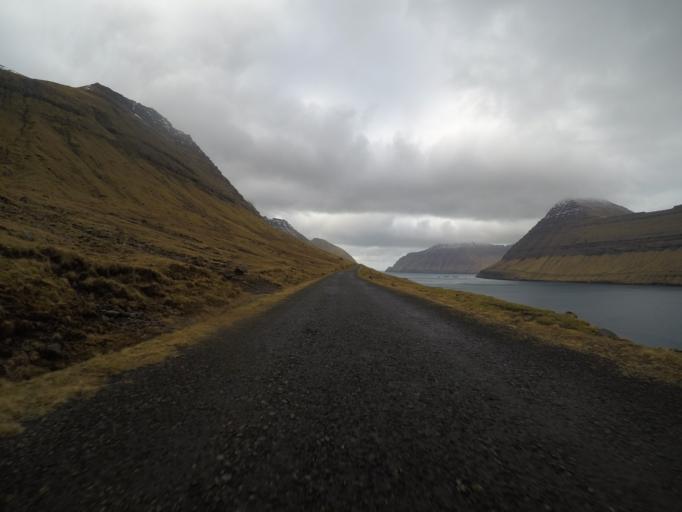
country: FO
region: Nordoyar
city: Klaksvik
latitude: 62.3186
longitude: -6.5582
